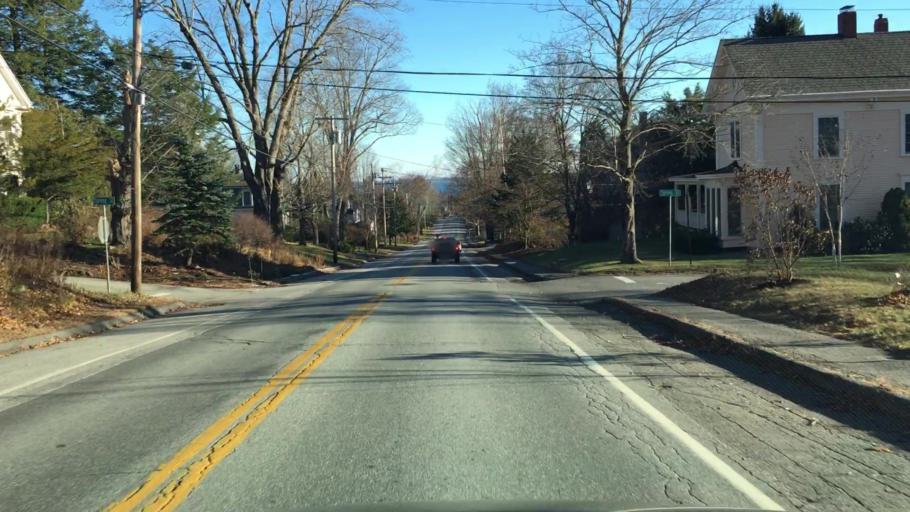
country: US
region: Maine
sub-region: Knox County
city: Camden
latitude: 44.2155
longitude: -69.0702
